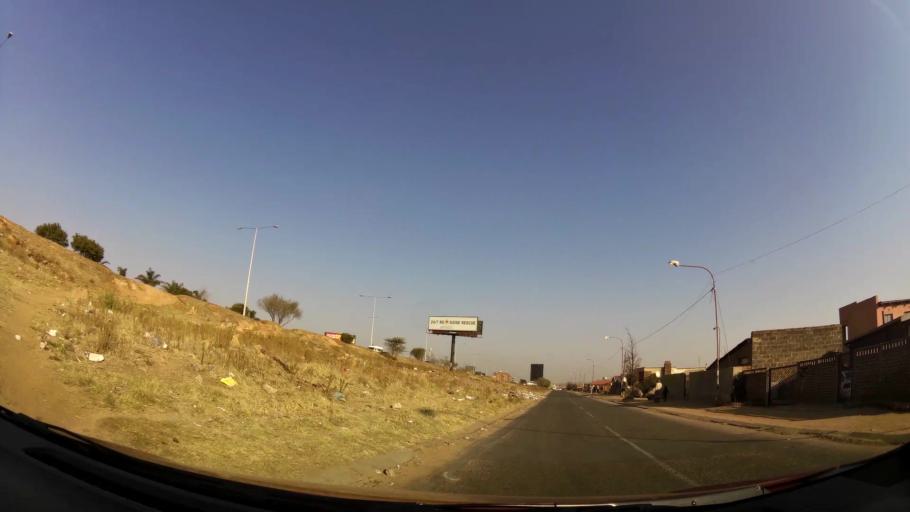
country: ZA
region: Gauteng
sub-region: City of Johannesburg Metropolitan Municipality
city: Soweto
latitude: -26.2602
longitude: 27.9510
